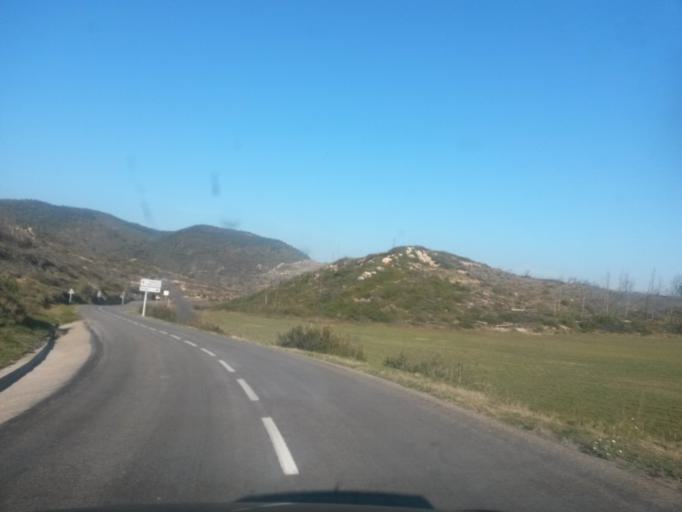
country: ES
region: Catalonia
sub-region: Provincia de Girona
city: Biure
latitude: 42.3370
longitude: 2.8715
